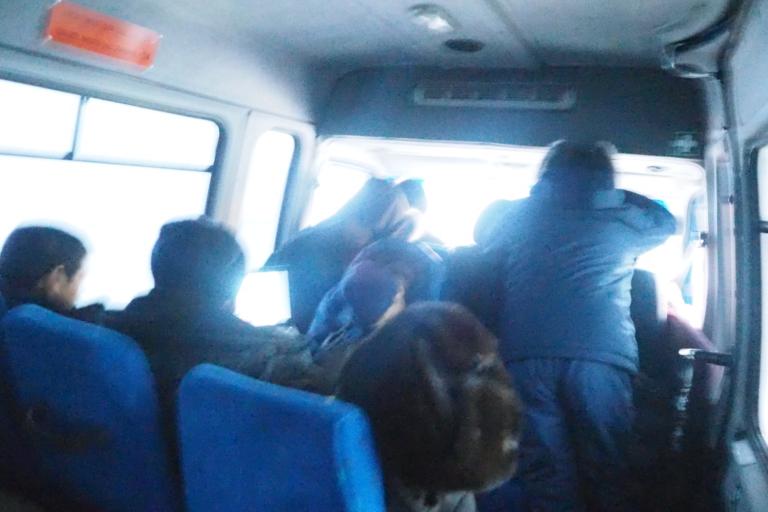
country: RU
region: Altai Krai
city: Zonal'noye
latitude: 52.8569
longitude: 84.8545
